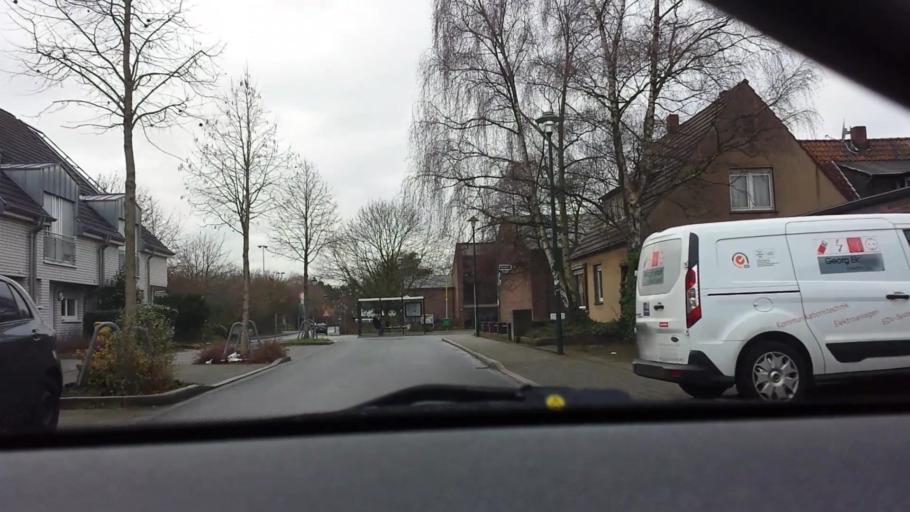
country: DE
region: North Rhine-Westphalia
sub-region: Regierungsbezirk Dusseldorf
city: Dusseldorf
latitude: 51.1846
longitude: 6.8150
